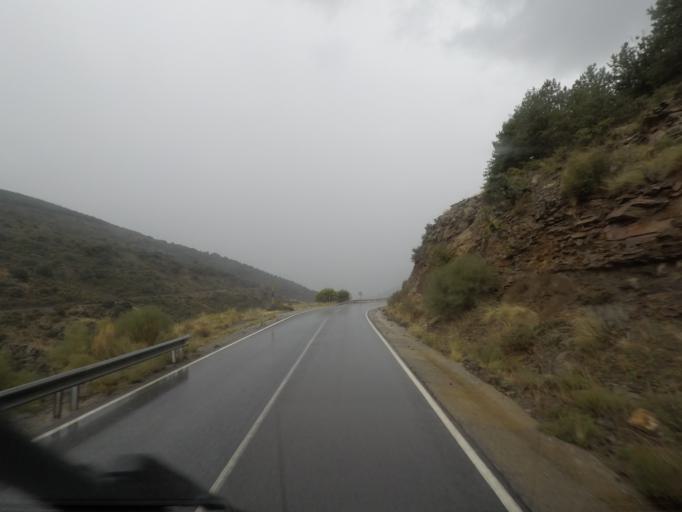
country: ES
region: Andalusia
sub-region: Provincia de Almeria
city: Bayarcal
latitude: 37.0706
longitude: -3.0177
